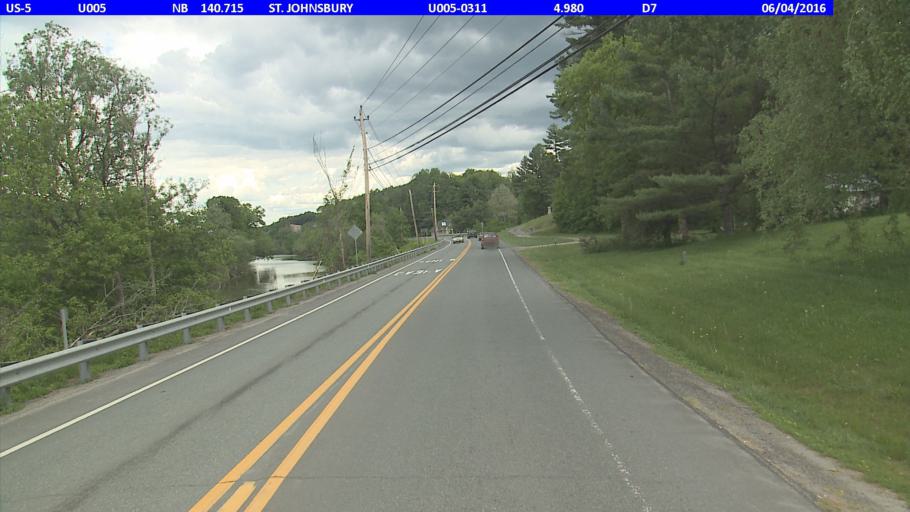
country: US
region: Vermont
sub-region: Caledonia County
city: St Johnsbury
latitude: 44.4628
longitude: -72.0147
